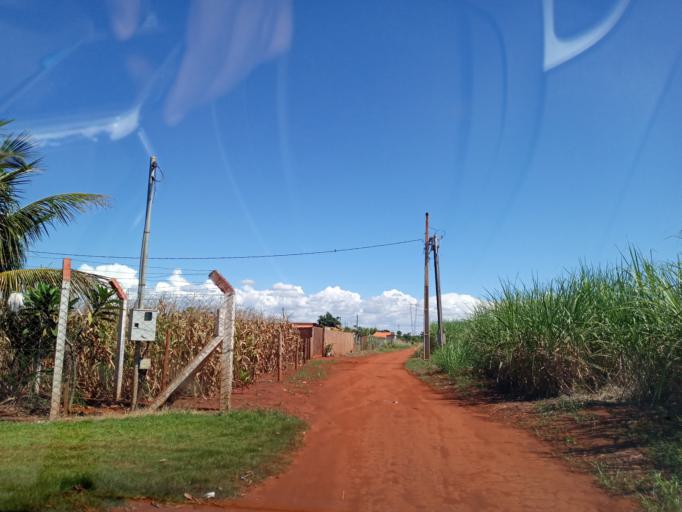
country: BR
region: Goias
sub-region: Itumbiara
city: Itumbiara
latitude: -18.4313
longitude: -49.1171
